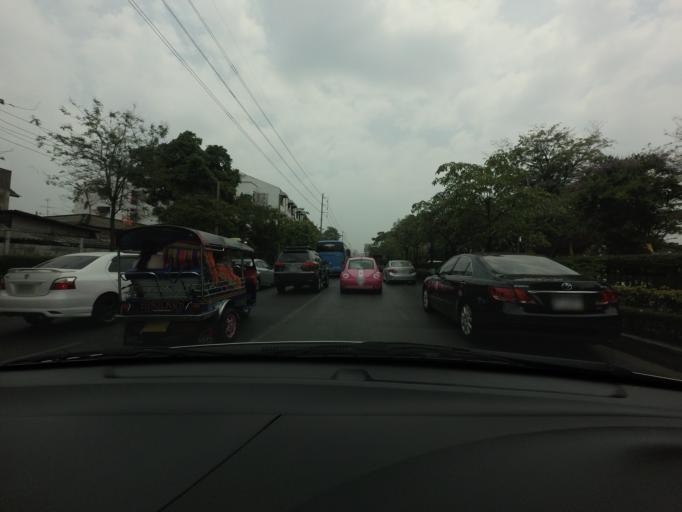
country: TH
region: Bangkok
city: Pom Prap Sattru Phai
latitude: 13.7599
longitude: 100.5175
